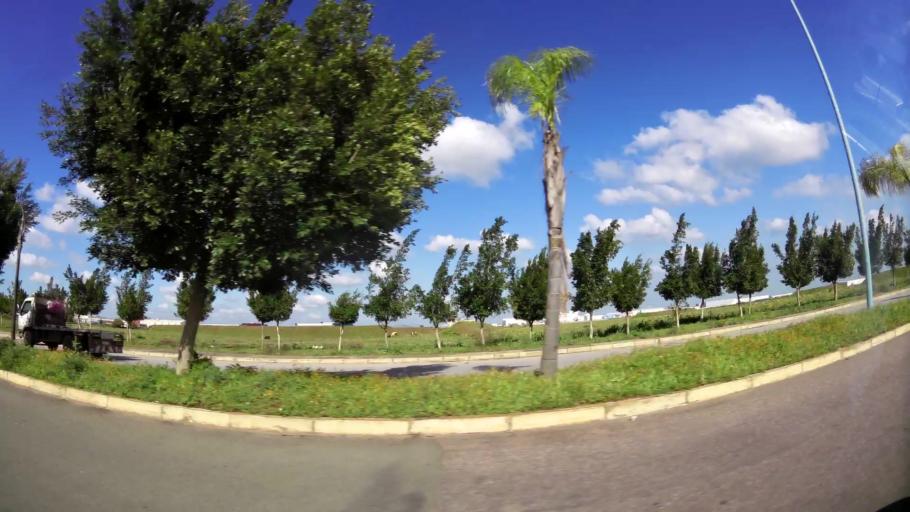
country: MA
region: Grand Casablanca
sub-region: Mediouna
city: Mediouna
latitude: 33.3992
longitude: -7.5549
